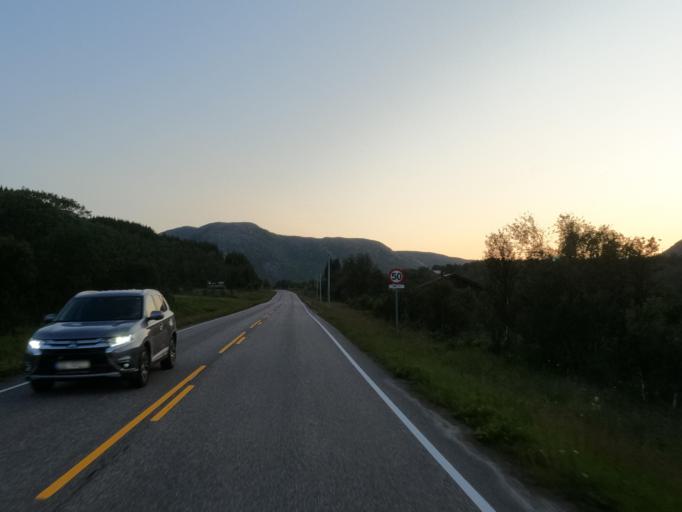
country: NO
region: Nordland
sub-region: Tjeldsund
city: Hol
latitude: 68.5647
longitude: 16.2874
